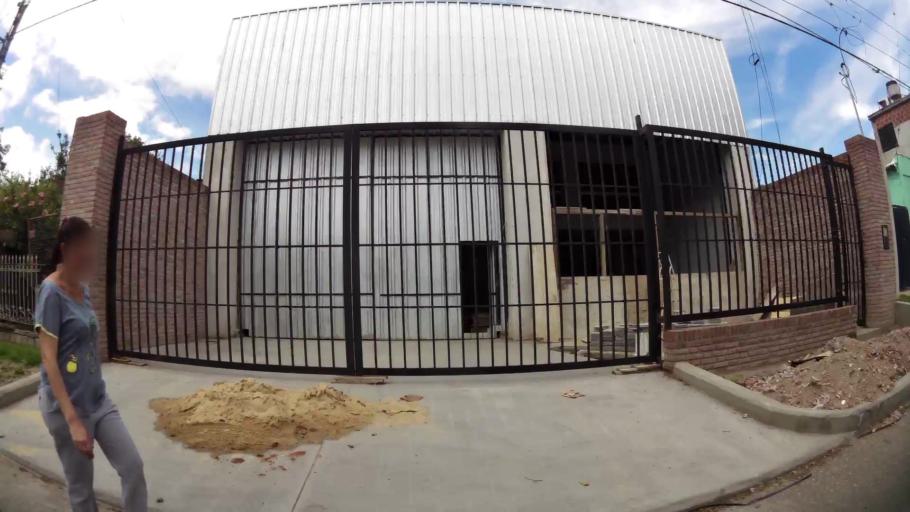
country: AR
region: Santa Fe
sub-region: Departamento de Rosario
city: Rosario
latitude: -32.9709
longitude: -60.6260
